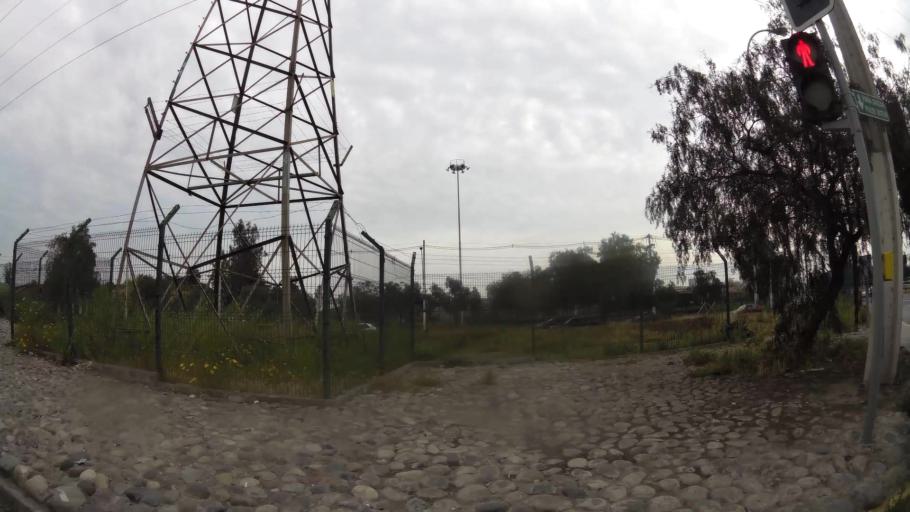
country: CL
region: Santiago Metropolitan
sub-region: Provincia de Santiago
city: Villa Presidente Frei, Nunoa, Santiago, Chile
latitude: -33.4957
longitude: -70.6070
